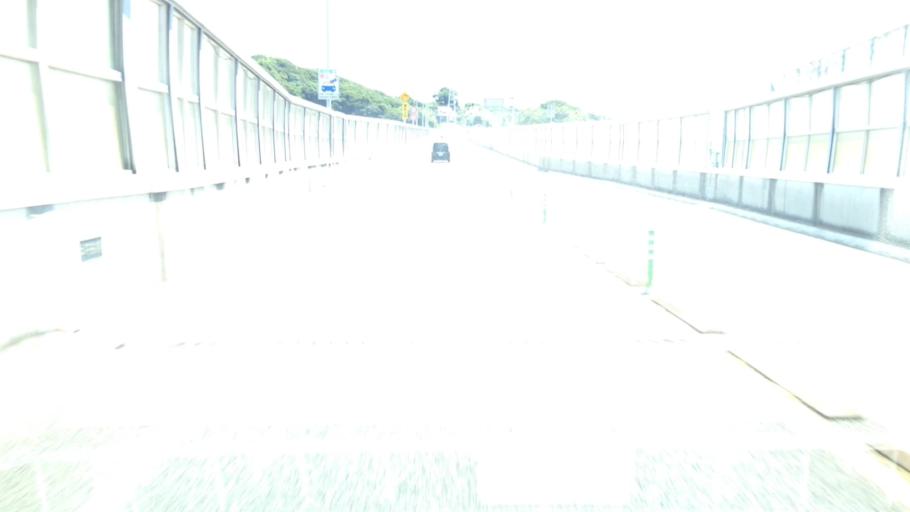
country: JP
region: Kanagawa
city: Yokosuka
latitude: 35.2212
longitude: 139.6369
